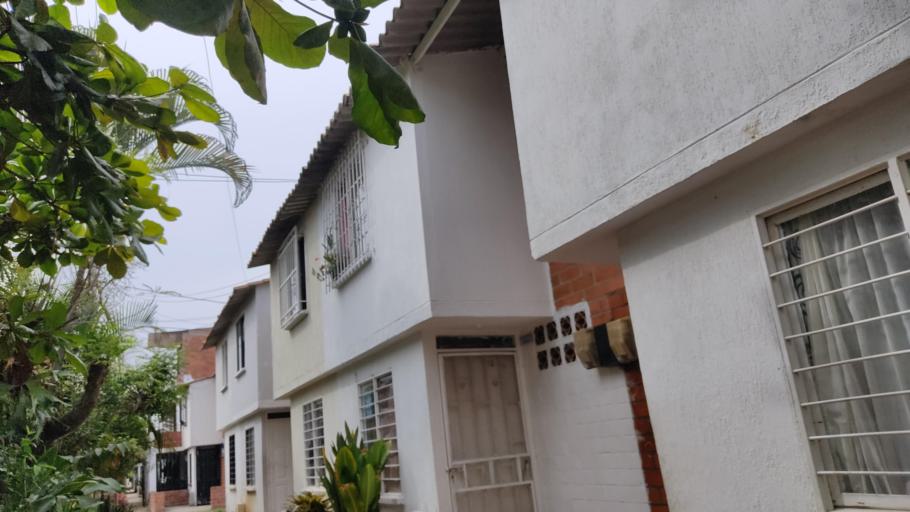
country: CO
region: Valle del Cauca
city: Jamundi
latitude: 3.2389
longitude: -76.5113
